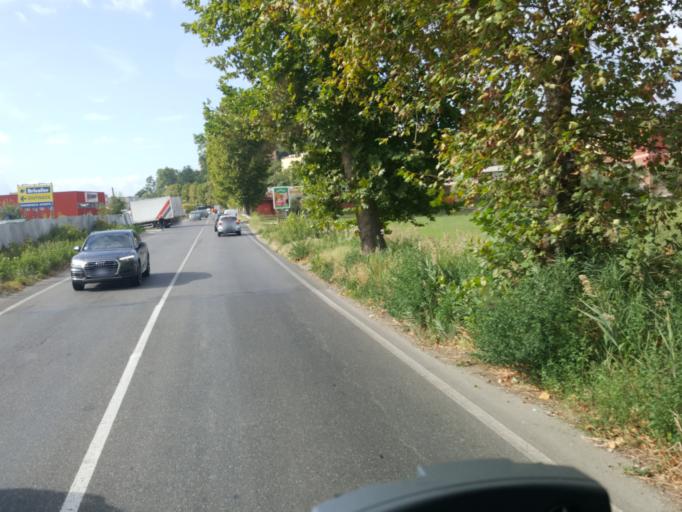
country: IT
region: Latium
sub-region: Citta metropolitana di Roma Capitale
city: Girardi-Bellavista-Terrazze
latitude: 42.1087
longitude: 12.5838
